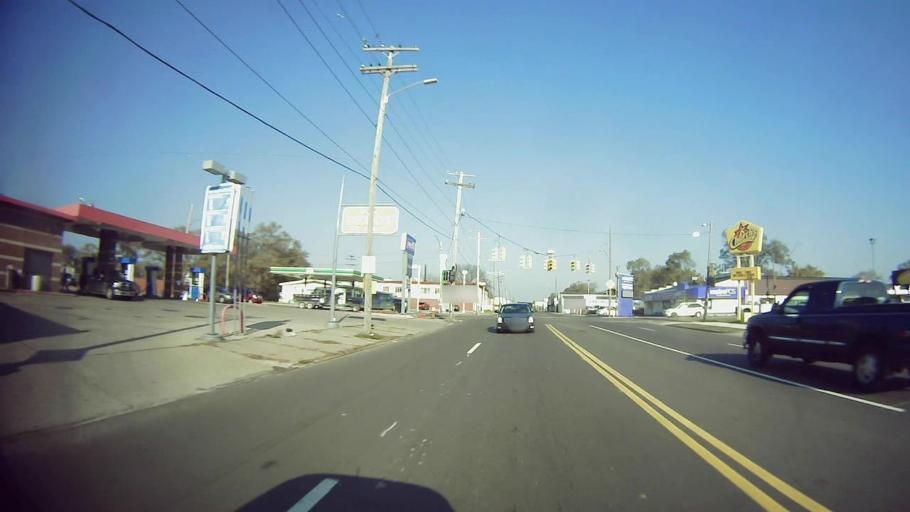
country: US
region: Michigan
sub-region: Oakland County
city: Oak Park
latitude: 42.4017
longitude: -83.1792
